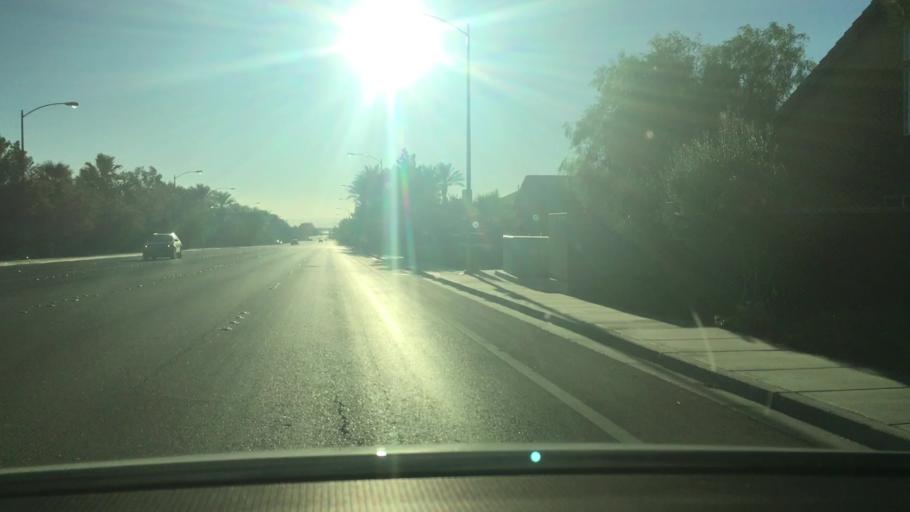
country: US
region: Nevada
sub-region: Clark County
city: Summerlin South
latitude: 36.0775
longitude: -115.3128
